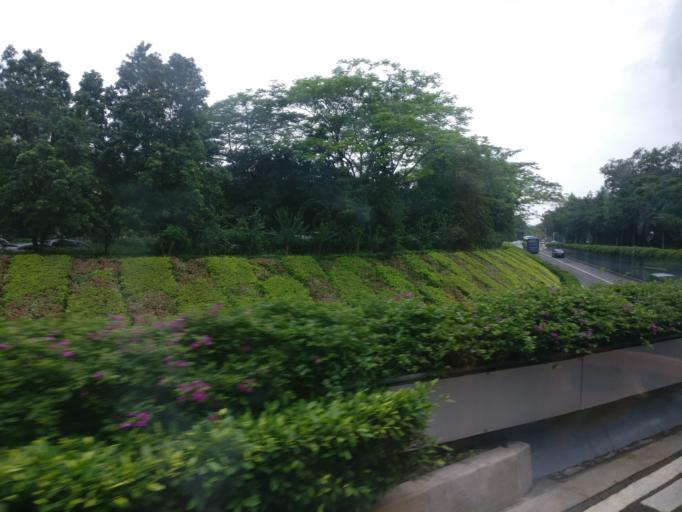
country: CN
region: Guangdong
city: Huangshi
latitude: 23.1865
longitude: 113.2747
